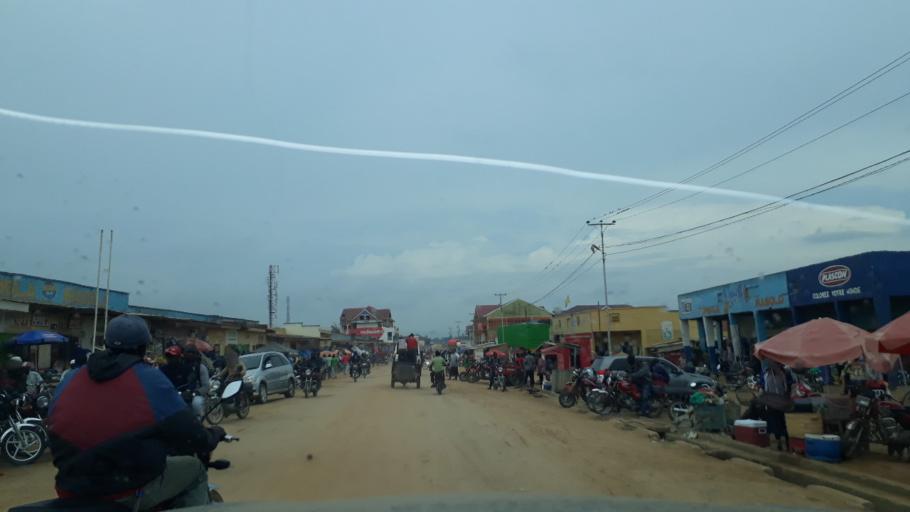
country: CD
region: Eastern Province
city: Bunia
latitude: 1.5680
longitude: 30.2476
